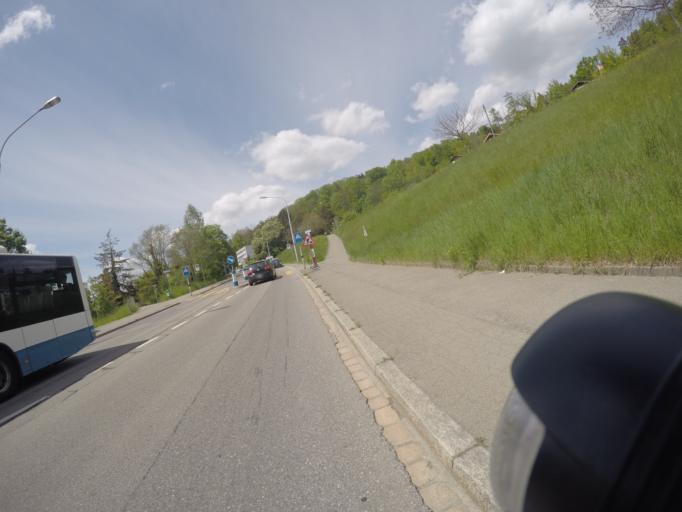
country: CH
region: Zurich
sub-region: Bezirk Zuerich
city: Zuerich (Kreis 10) / Wipkingen
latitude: 47.3996
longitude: 8.5207
